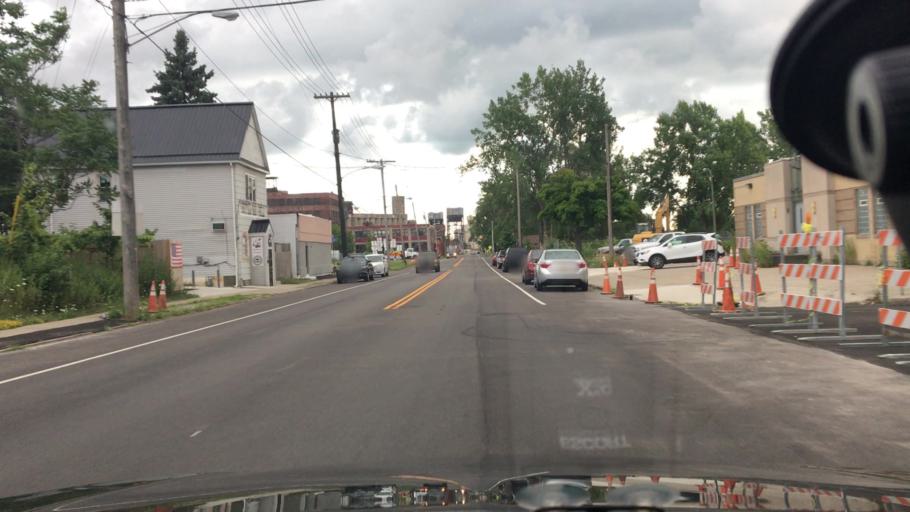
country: US
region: New York
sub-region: Erie County
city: Buffalo
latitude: 42.8704
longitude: -78.8650
